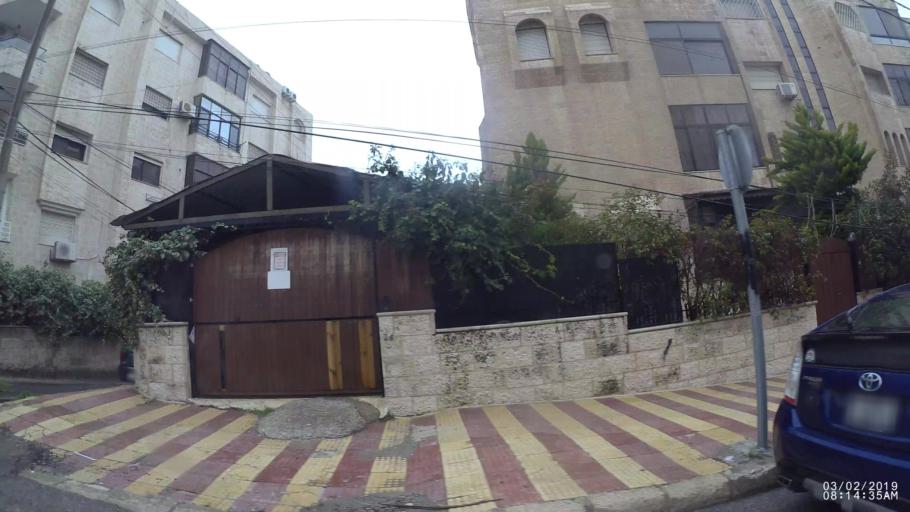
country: JO
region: Amman
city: Wadi as Sir
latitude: 31.9674
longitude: 35.8655
